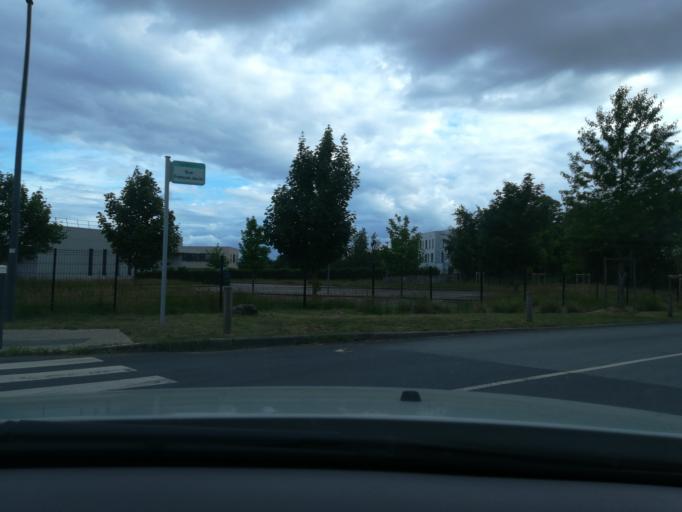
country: FR
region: Haute-Normandie
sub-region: Departement de la Seine-Maritime
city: Isneauville
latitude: 49.4894
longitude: 1.1392
